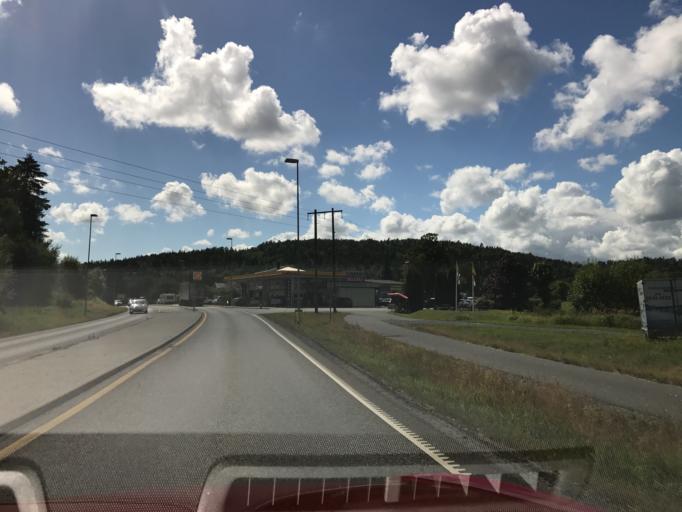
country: NO
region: Telemark
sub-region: Bamble
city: Langesund
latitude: 59.0124
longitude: 9.6676
